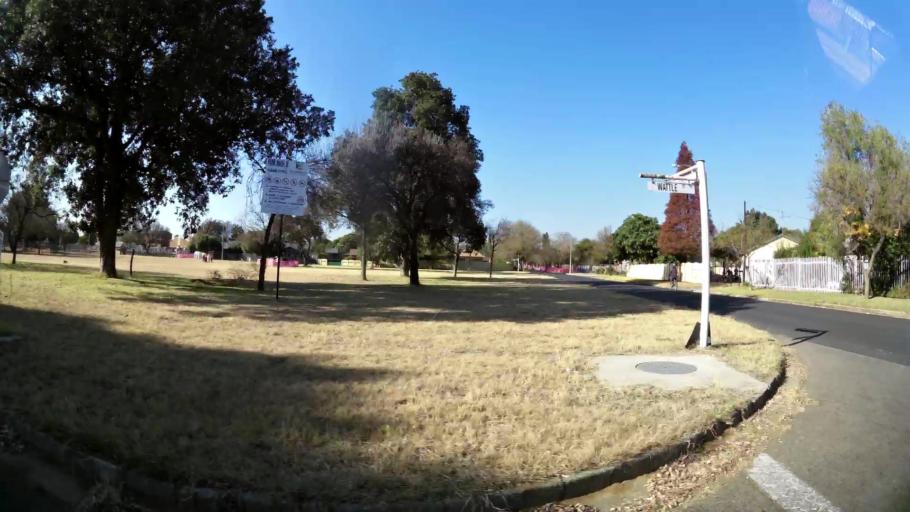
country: ZA
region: Gauteng
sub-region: Ekurhuleni Metropolitan Municipality
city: Benoni
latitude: -26.1521
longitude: 28.3026
